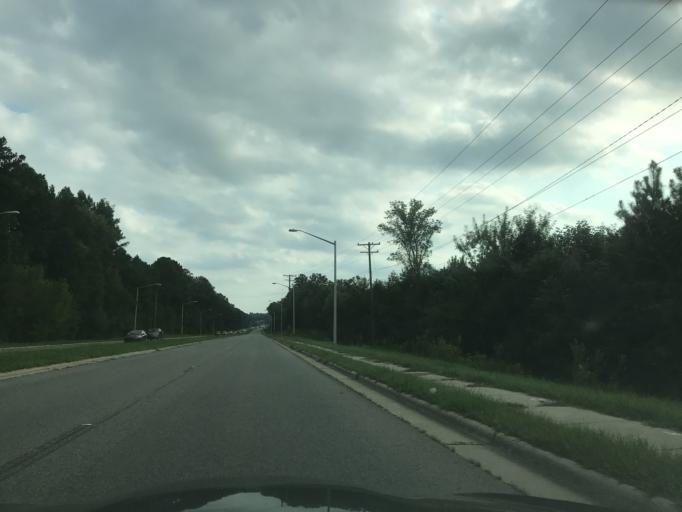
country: US
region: North Carolina
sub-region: Durham County
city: Durham
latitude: 35.9238
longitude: -78.8900
